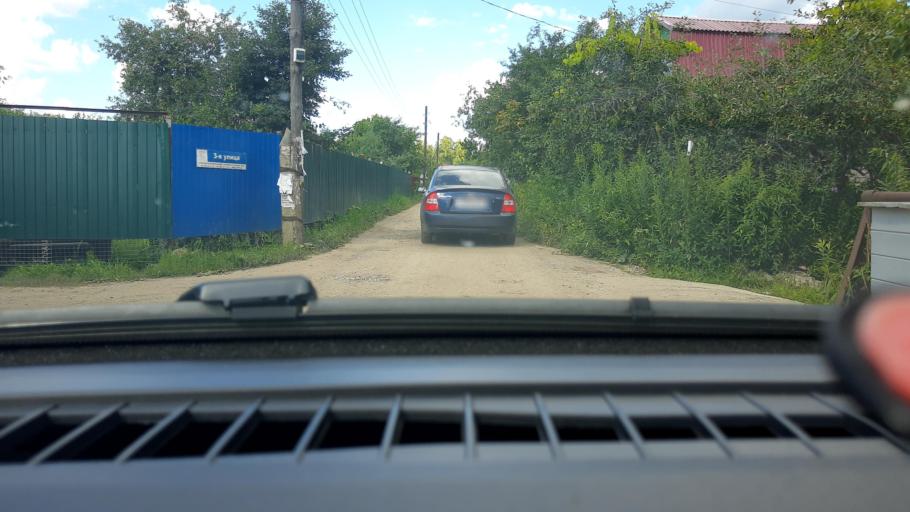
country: RU
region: Nizjnij Novgorod
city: Gorbatovka
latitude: 56.3199
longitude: 43.8289
